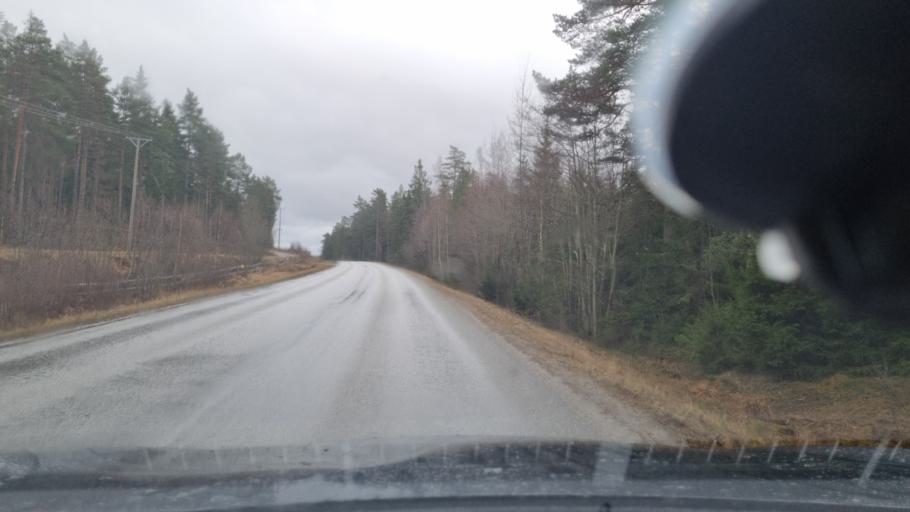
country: SE
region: Stockholm
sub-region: Sigtuna Kommun
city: Sigtuna
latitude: 59.5555
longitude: 17.7237
